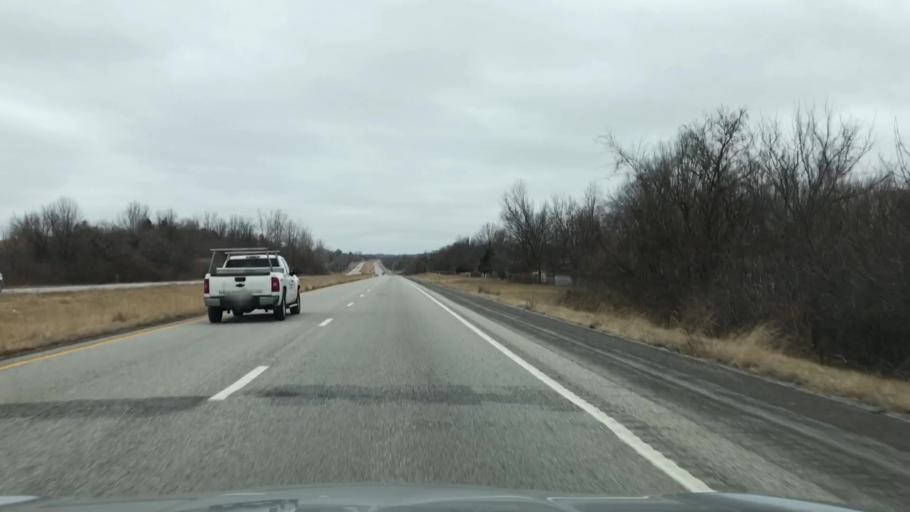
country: US
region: Missouri
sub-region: Clay County
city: Liberty
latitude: 39.2095
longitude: -94.4056
